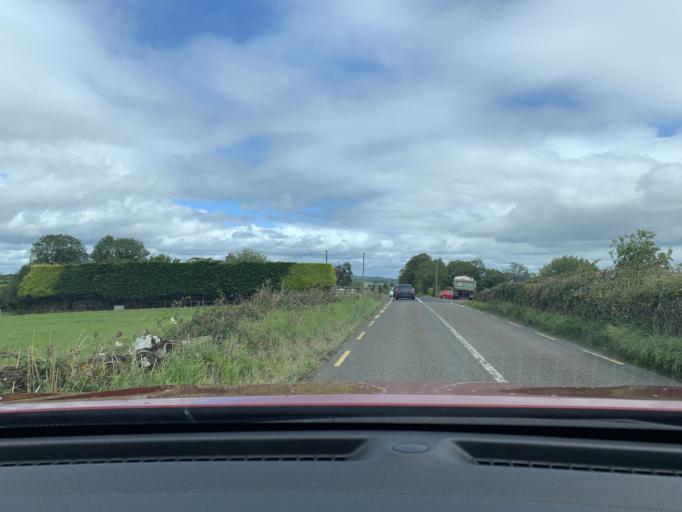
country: IE
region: Connaught
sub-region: County Leitrim
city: Carrick-on-Shannon
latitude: 53.9230
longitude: -8.1183
